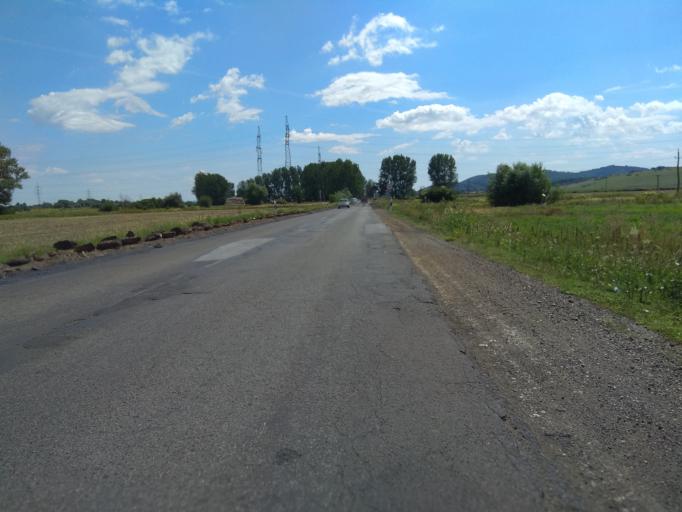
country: HU
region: Borsod-Abauj-Zemplen
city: Sajokaza
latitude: 48.2690
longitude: 20.5921
